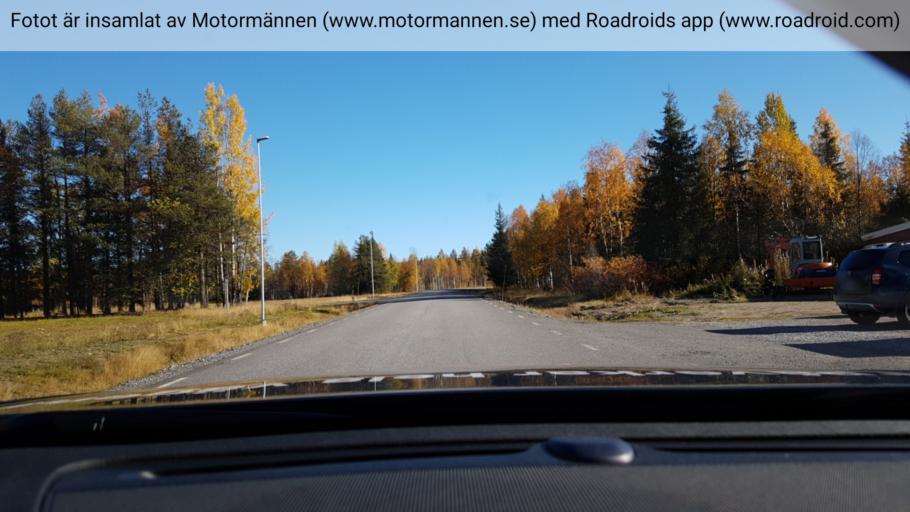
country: SE
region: Norrbotten
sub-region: Gallivare Kommun
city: Gaellivare
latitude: 66.7557
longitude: 20.9697
